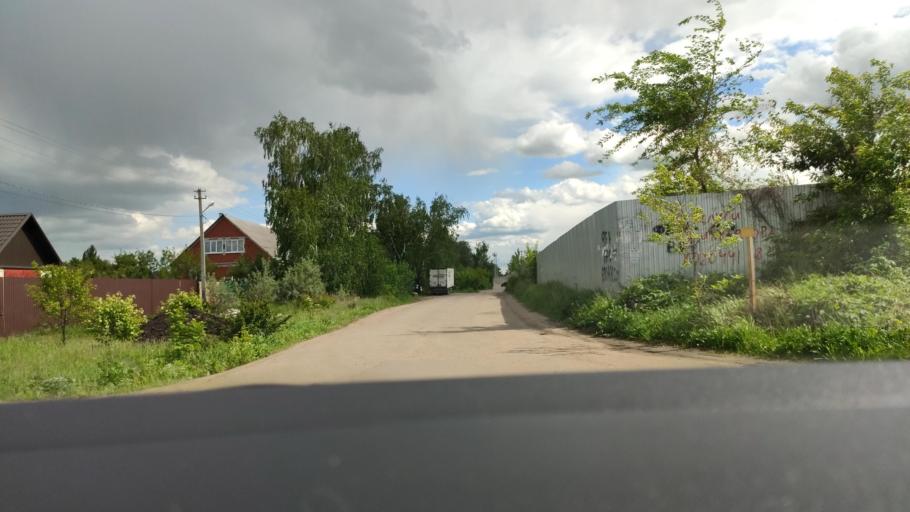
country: RU
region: Voronezj
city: Somovo
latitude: 51.6804
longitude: 39.3172
